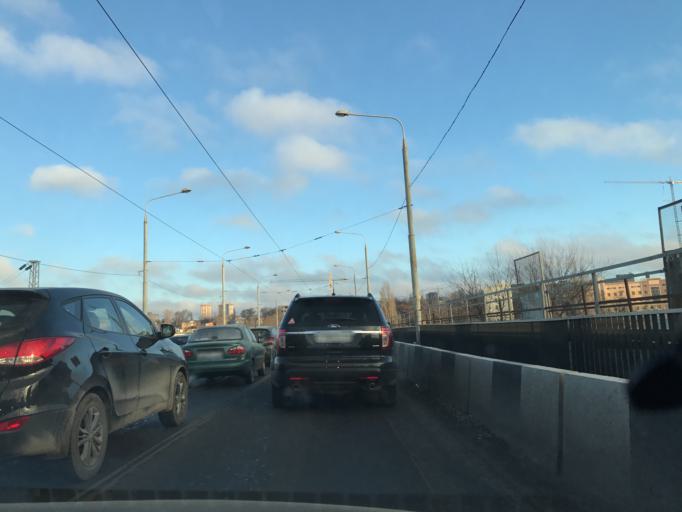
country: RU
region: Rostov
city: Rostov-na-Donu
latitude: 47.2220
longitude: 39.6853
